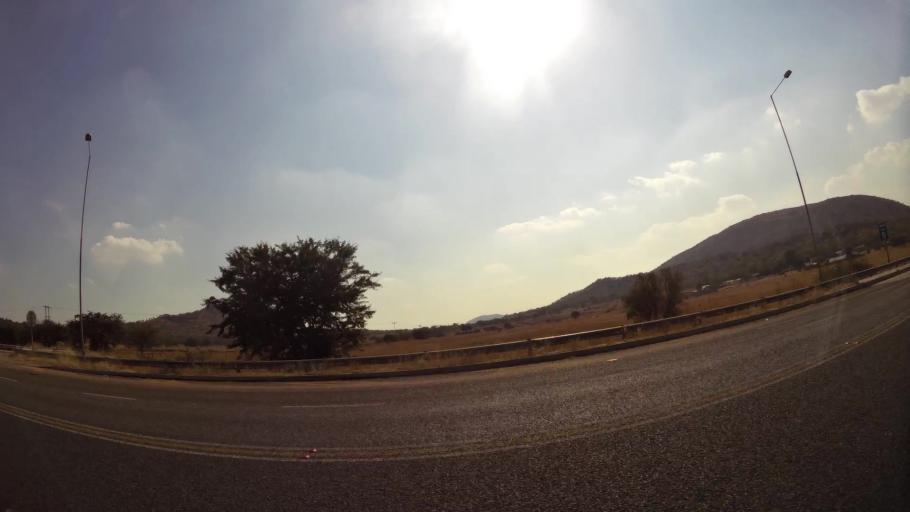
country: ZA
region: North-West
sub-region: Bojanala Platinum District Municipality
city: Rustenburg
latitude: -25.5829
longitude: 27.1333
